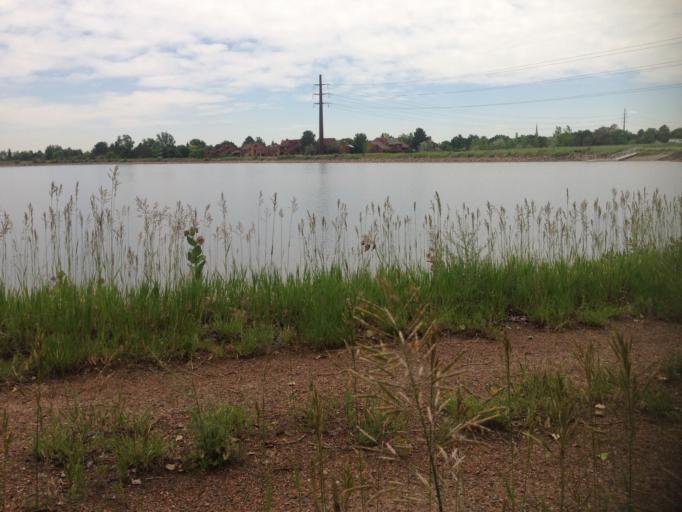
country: US
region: Colorado
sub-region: Boulder County
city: Louisville
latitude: 39.9913
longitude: -105.1584
